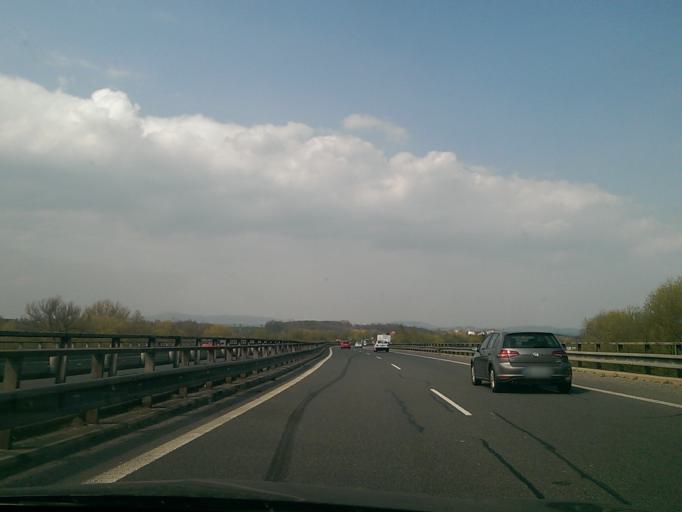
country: CZ
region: Central Bohemia
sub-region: Okres Mlada Boleslav
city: Zd'ar
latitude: 50.5490
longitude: 15.0432
